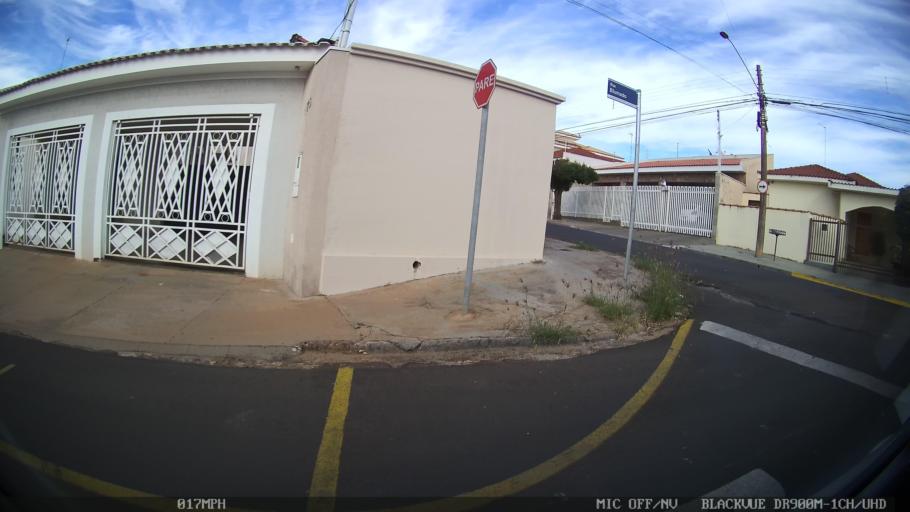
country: BR
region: Sao Paulo
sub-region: Catanduva
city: Catanduva
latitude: -21.1378
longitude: -48.9912
